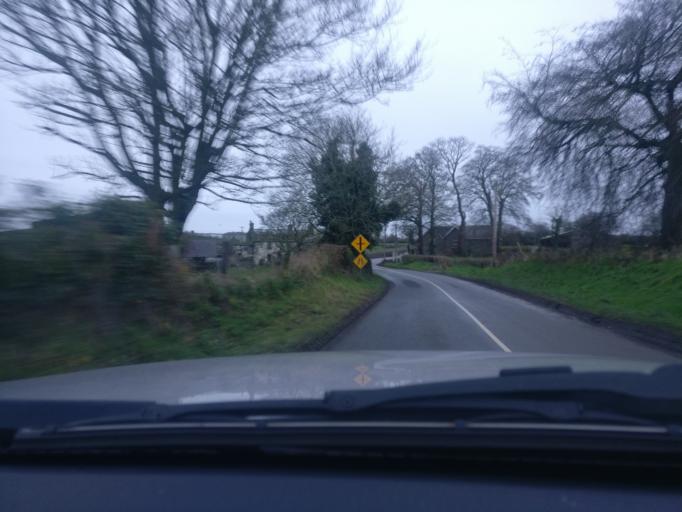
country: IE
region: Leinster
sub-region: An Mhi
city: Dunshaughlin
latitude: 53.4868
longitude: -6.6097
